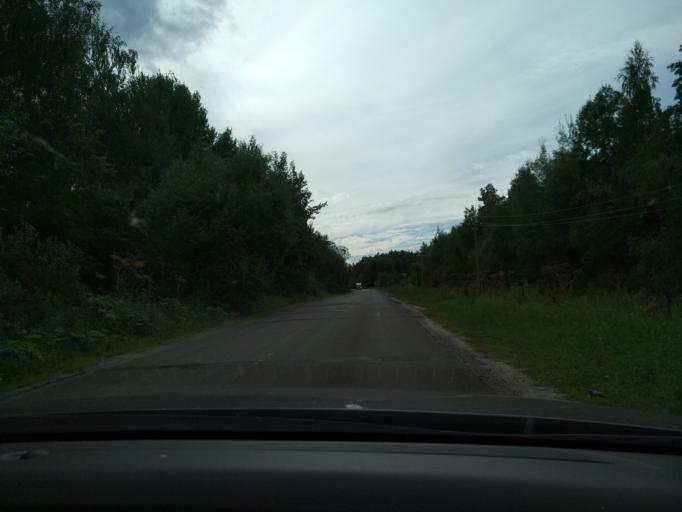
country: RU
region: Moskovskaya
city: Krasnyy Tkach
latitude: 55.3797
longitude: 39.2149
